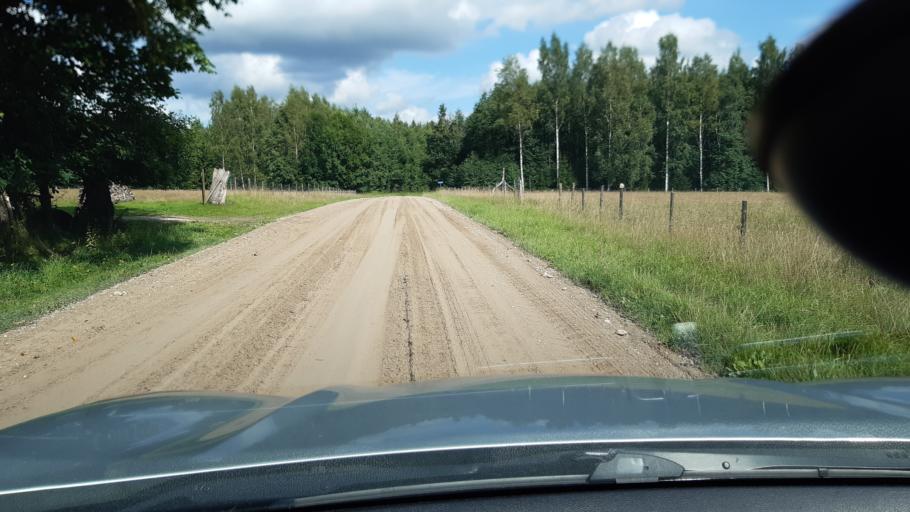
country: EE
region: Jaervamaa
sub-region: Tueri vald
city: Tueri
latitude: 58.9217
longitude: 25.2001
